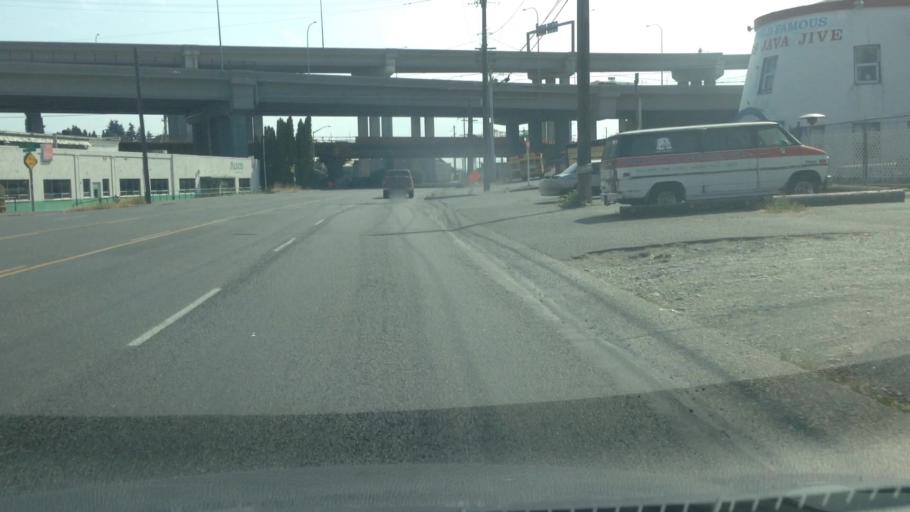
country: US
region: Washington
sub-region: Pierce County
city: Tacoma
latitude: 47.2320
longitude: -122.4648
